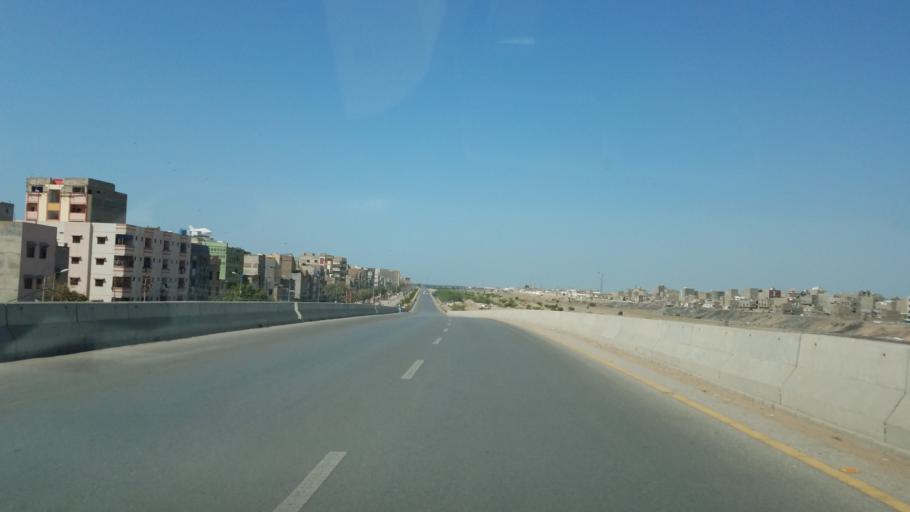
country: PK
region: Sindh
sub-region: Karachi District
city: Karachi
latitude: 24.8797
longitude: 66.9951
